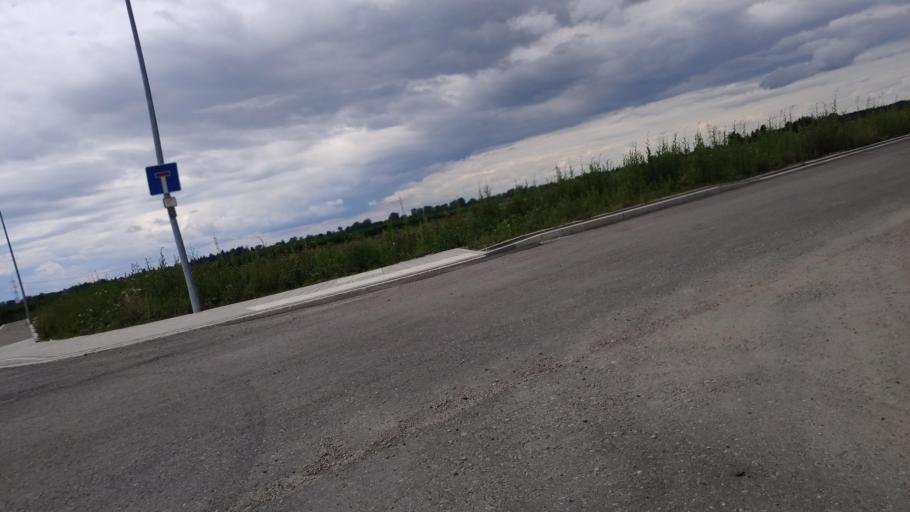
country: DE
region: Bavaria
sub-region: Swabia
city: Mering
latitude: 48.2721
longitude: 10.9705
